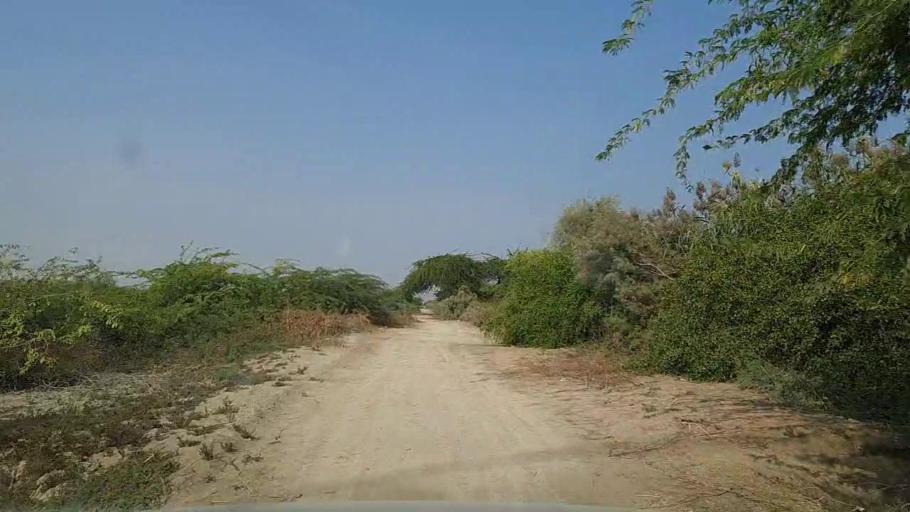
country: PK
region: Sindh
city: Mirpur Sakro
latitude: 24.5527
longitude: 67.5566
